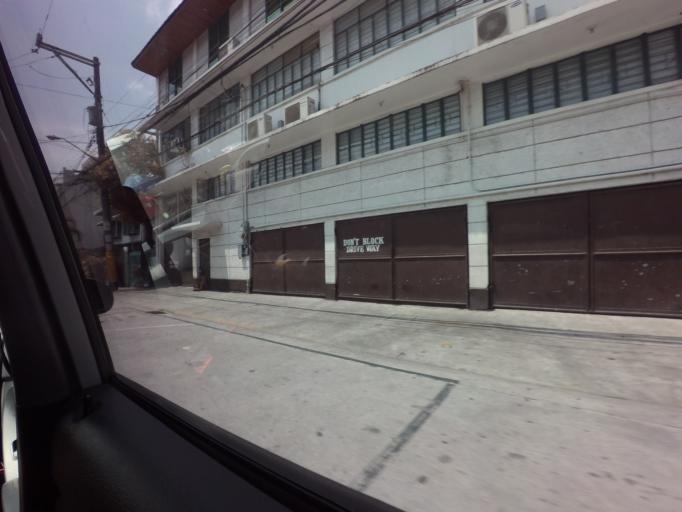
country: PH
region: Metro Manila
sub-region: City of Manila
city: Quiapo
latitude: 14.5866
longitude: 121.0034
